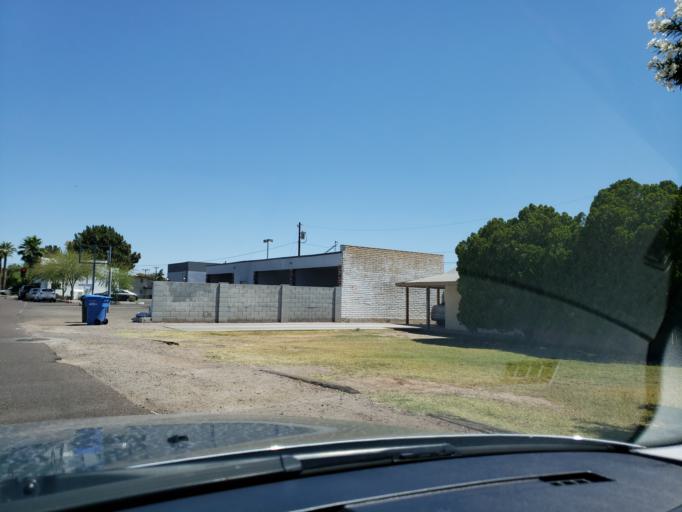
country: US
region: Arizona
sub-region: Maricopa County
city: Phoenix
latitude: 33.5084
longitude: -112.0869
